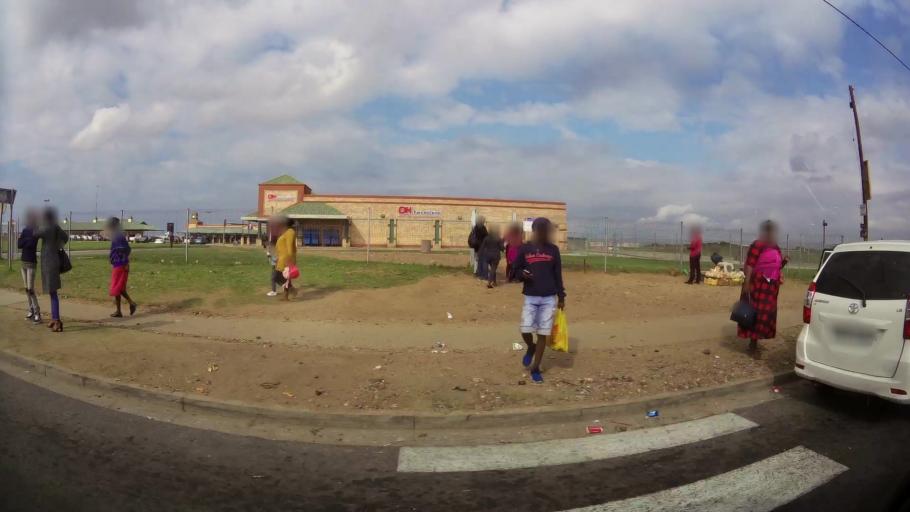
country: ZA
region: Eastern Cape
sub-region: Nelson Mandela Bay Metropolitan Municipality
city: Port Elizabeth
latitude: -33.8102
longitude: 25.5933
